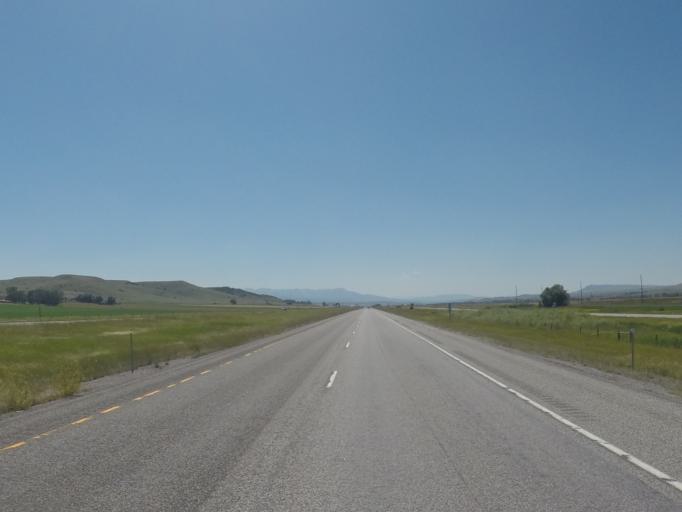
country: US
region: Montana
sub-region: Sweet Grass County
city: Big Timber
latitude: 45.8138
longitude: -110.0020
